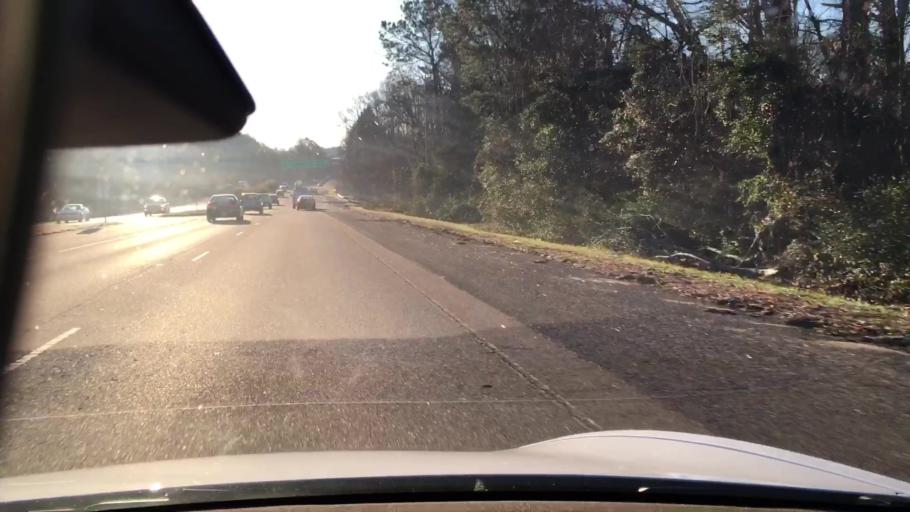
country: US
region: Virginia
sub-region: Chesterfield County
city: Bon Air
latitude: 37.5408
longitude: -77.5334
